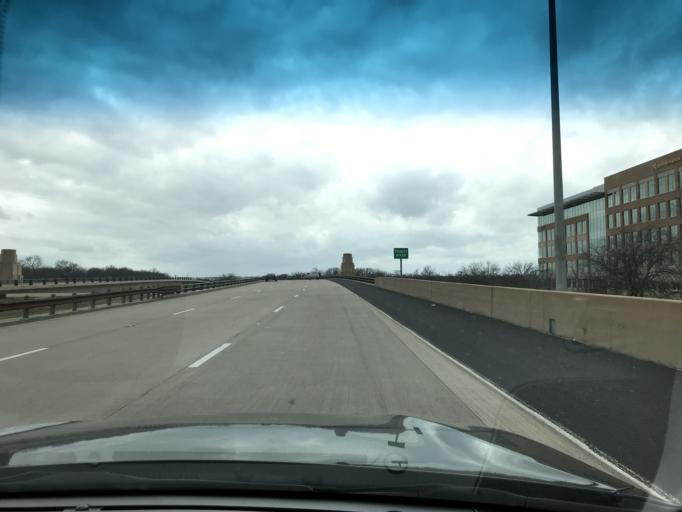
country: US
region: Texas
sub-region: Tarrant County
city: Westworth
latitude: 32.7083
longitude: -97.4042
